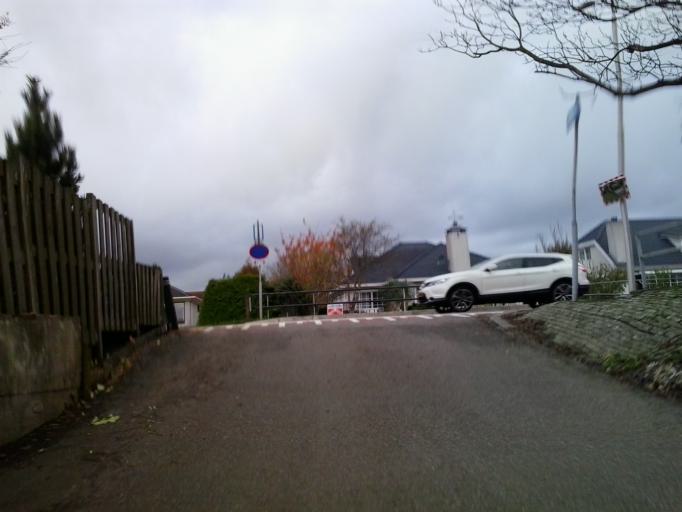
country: NL
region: South Holland
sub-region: Gemeente Lansingerland
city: Berkel en Rodenrijs
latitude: 51.9885
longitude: 4.4717
